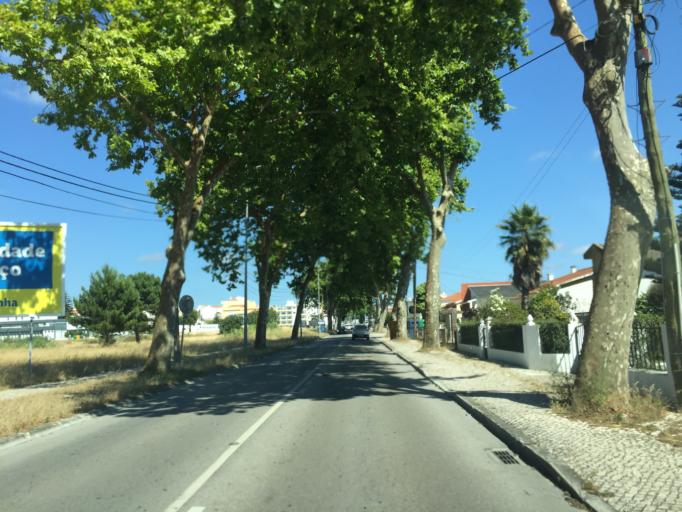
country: PT
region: Leiria
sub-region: Caldas da Rainha
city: Caldas da Rainha
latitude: 39.4059
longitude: -9.1510
